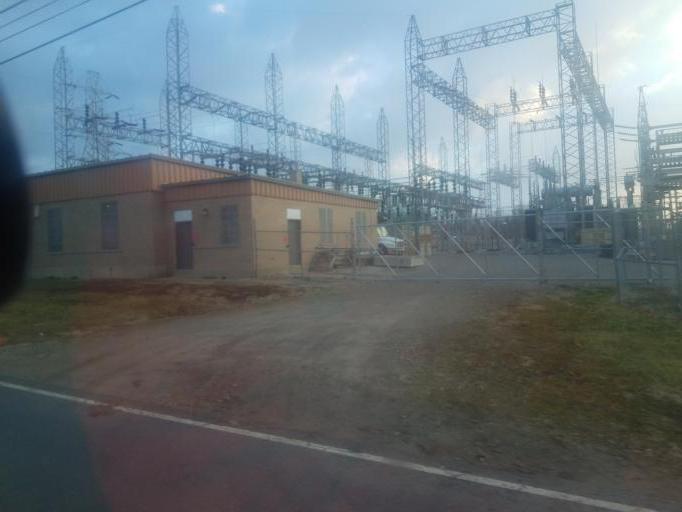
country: US
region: Ohio
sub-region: Marion County
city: Marion
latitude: 40.6010
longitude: -83.1547
